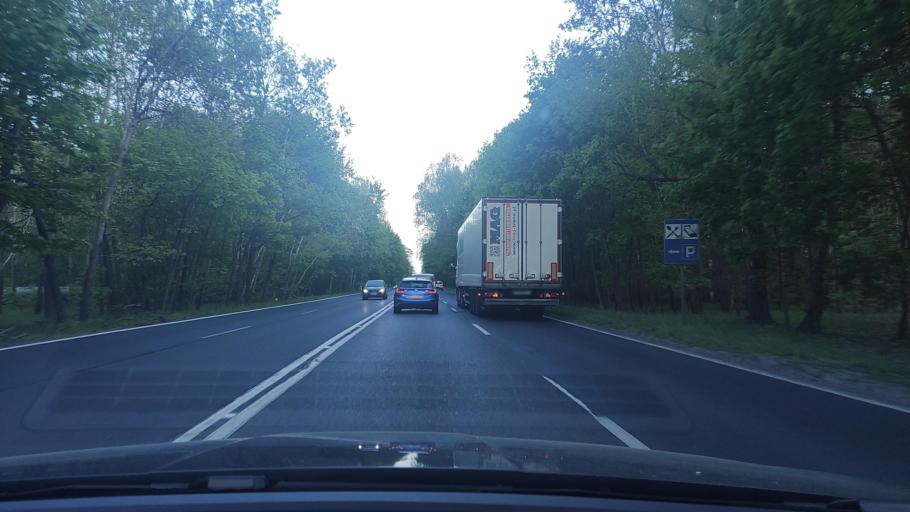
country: PL
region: Greater Poland Voivodeship
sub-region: Powiat poznanski
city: Czerwonak
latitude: 52.4235
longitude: 17.0156
